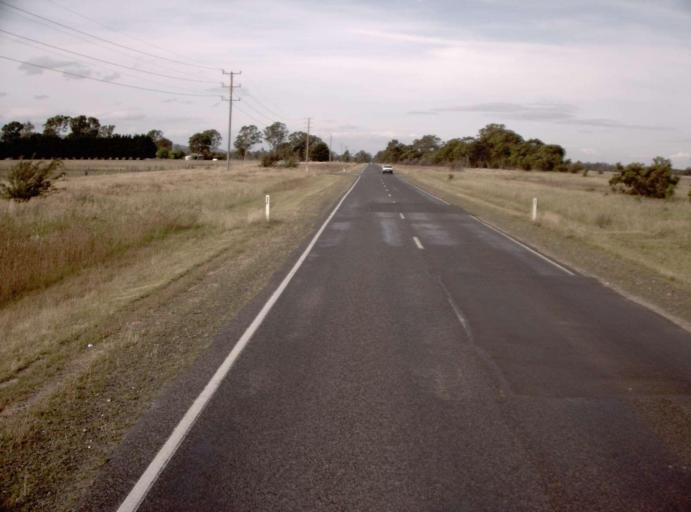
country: AU
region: Victoria
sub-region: Latrobe
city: Traralgon
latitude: -38.0817
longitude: 146.6074
